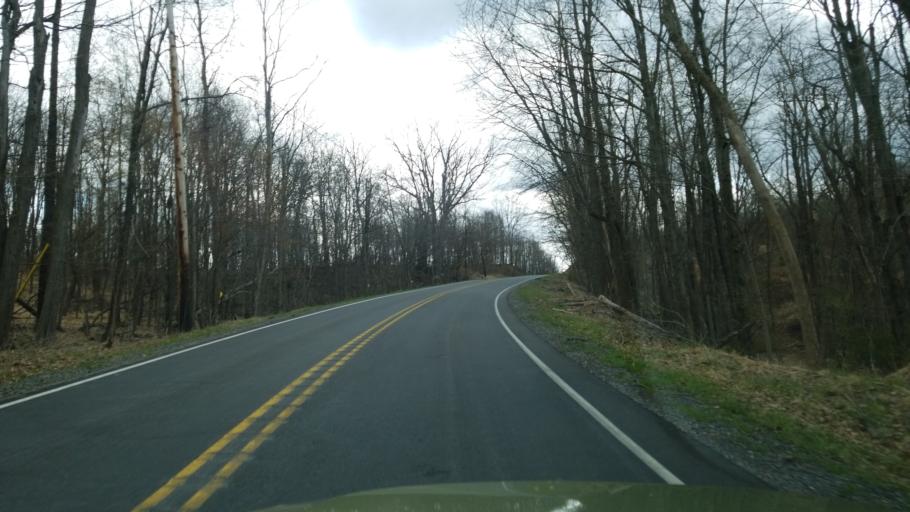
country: US
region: Pennsylvania
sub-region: Clearfield County
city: Curwensville
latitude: 40.8755
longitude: -78.4575
